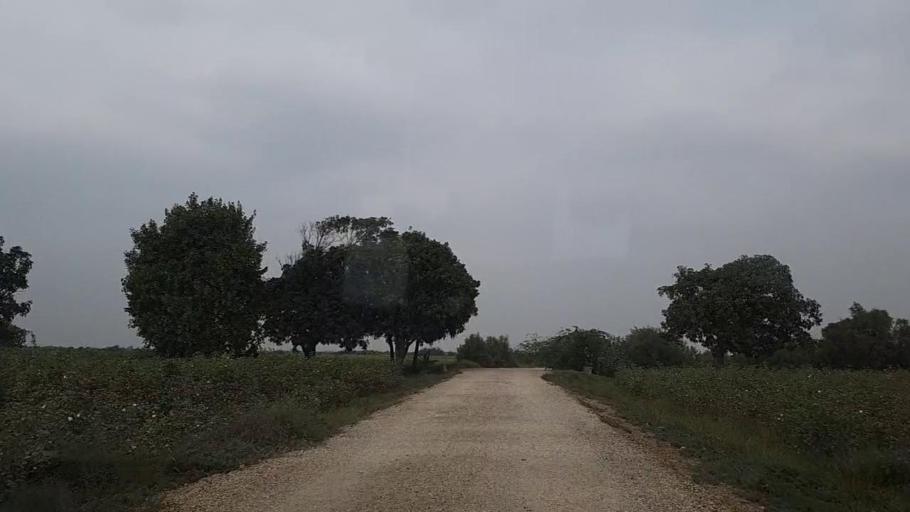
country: PK
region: Sindh
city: Mirpur Sakro
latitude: 24.6206
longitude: 67.7173
